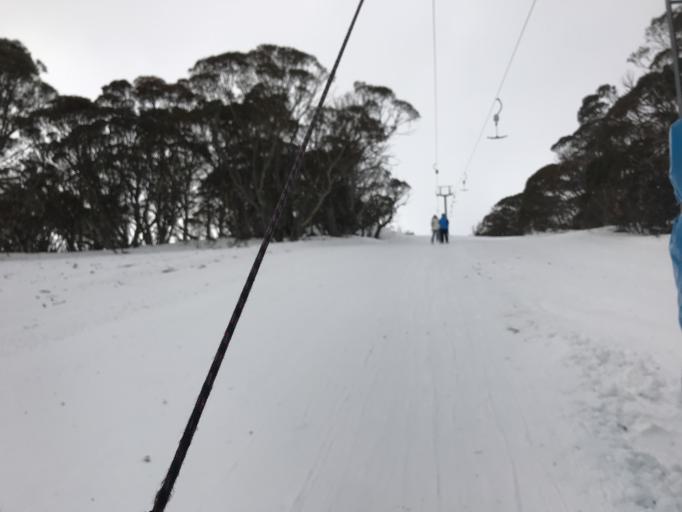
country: AU
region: New South Wales
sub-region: Snowy River
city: Jindabyne
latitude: -36.3836
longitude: 148.3754
